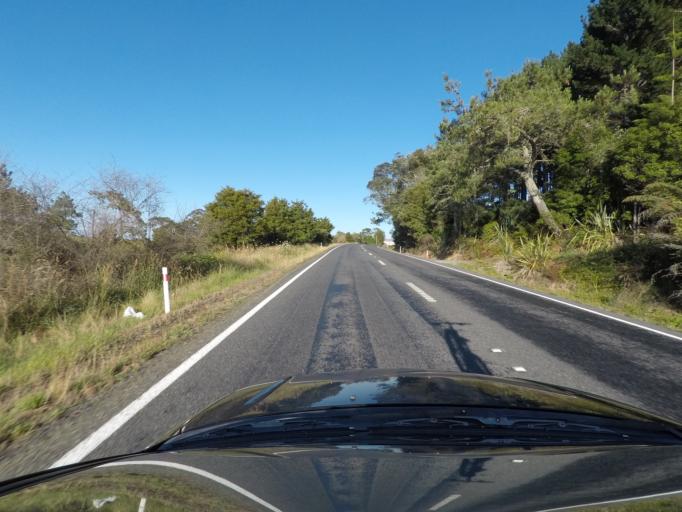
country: NZ
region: Northland
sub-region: Far North District
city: Kawakawa
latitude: -35.4945
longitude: 174.1404
